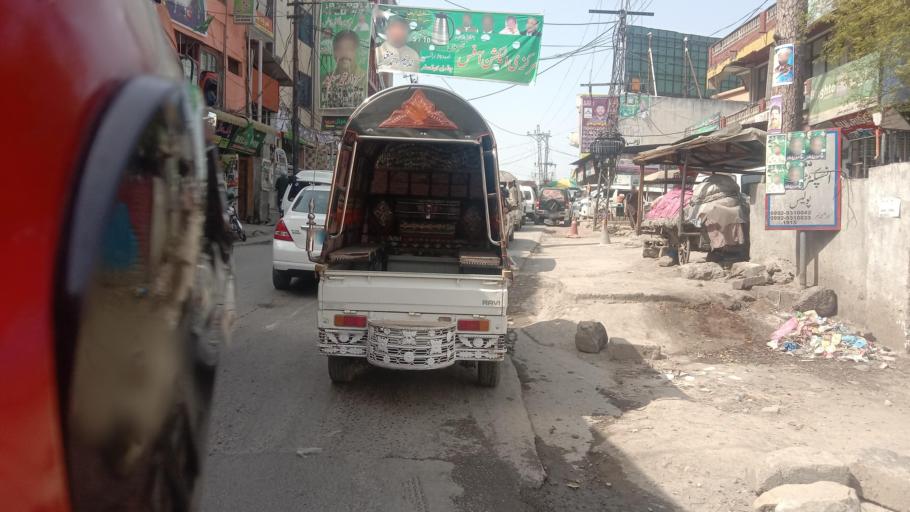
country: PK
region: Khyber Pakhtunkhwa
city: Abbottabad
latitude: 34.1407
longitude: 73.2137
